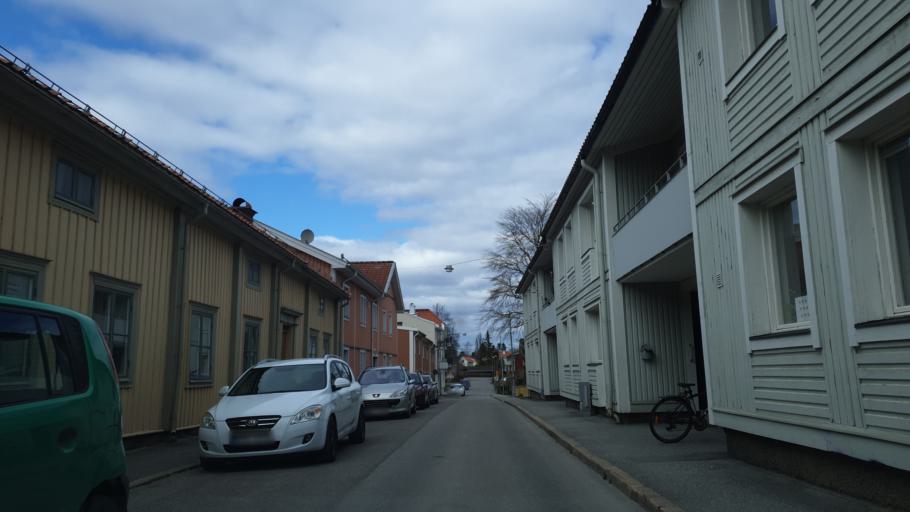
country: SE
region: OErebro
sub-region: Nora Kommun
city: Nora
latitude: 59.5210
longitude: 15.0416
